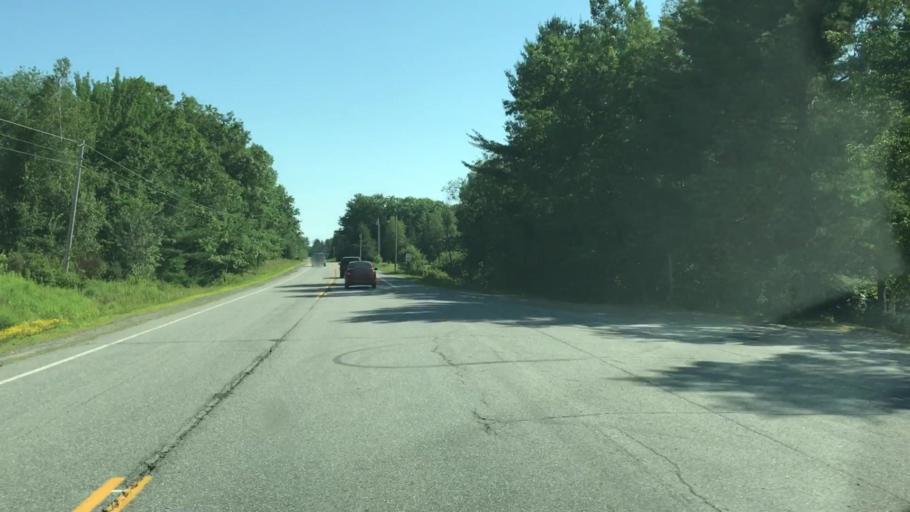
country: US
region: Maine
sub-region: Penobscot County
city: Enfield
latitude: 45.2953
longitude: -68.6208
